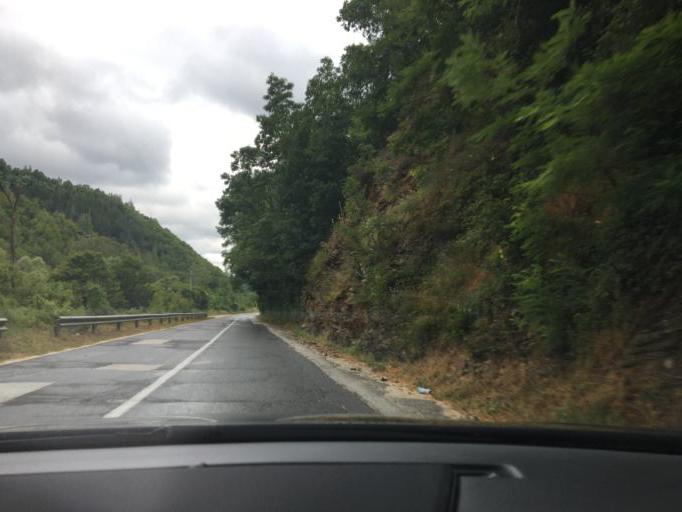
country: MK
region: Kriva Palanka
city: Kriva Palanka
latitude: 42.2246
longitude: 22.4175
